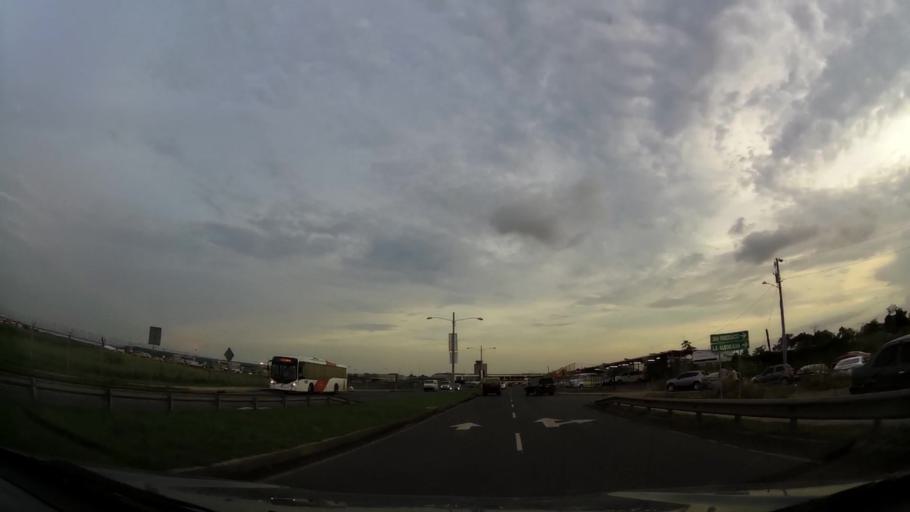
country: PA
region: Panama
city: Tocumen
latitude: 9.0728
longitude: -79.3895
